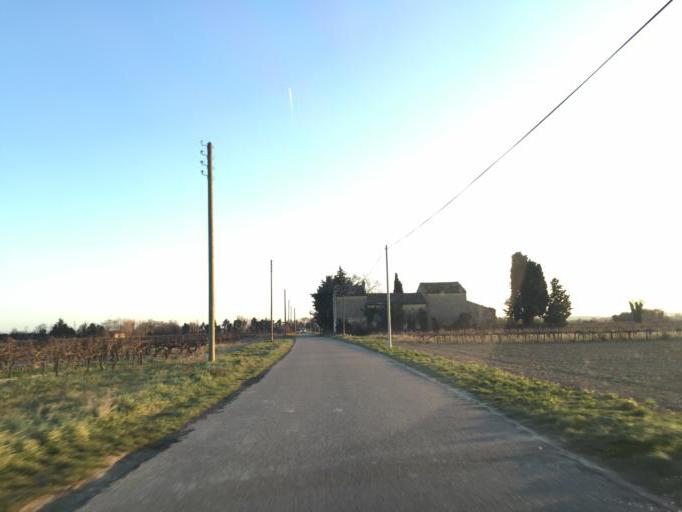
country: FR
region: Provence-Alpes-Cote d'Azur
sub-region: Departement du Vaucluse
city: Camaret-sur-Aigues
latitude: 44.1483
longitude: 4.8746
